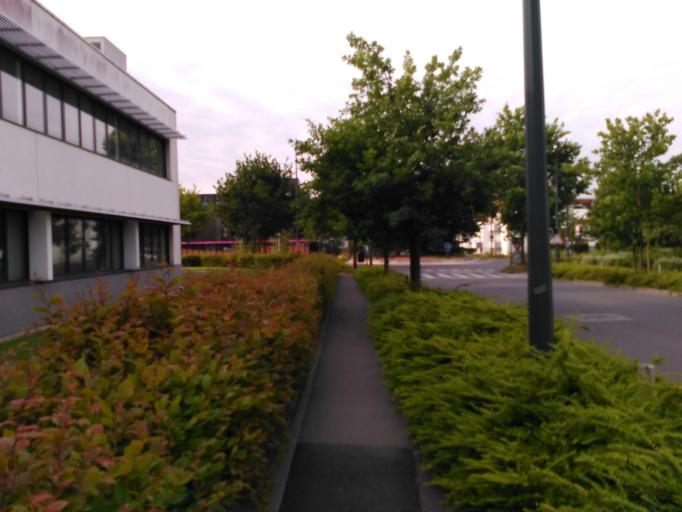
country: FR
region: Brittany
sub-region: Departement d'Ille-et-Vilaine
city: Vezin-le-Coquet
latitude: 48.1167
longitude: -1.7164
